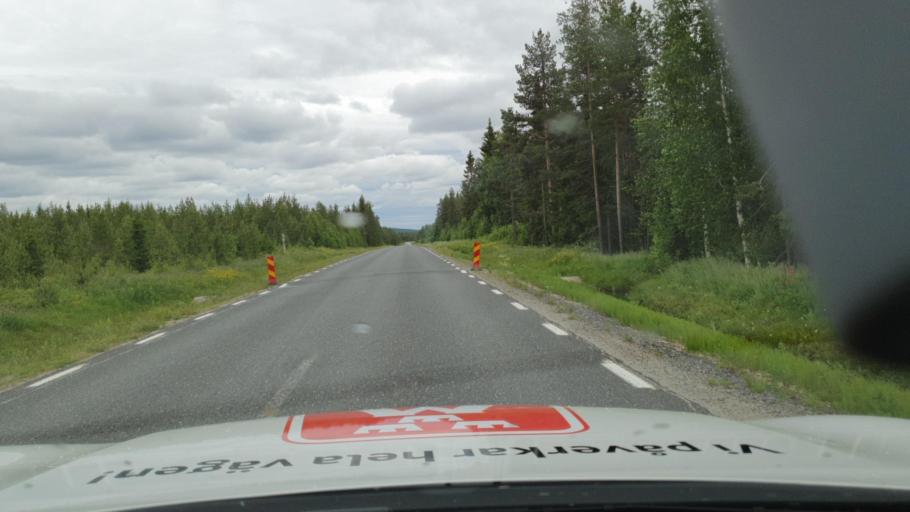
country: SE
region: Vaesterbotten
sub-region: Lycksele Kommun
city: Soderfors
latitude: 64.2812
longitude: 18.1924
